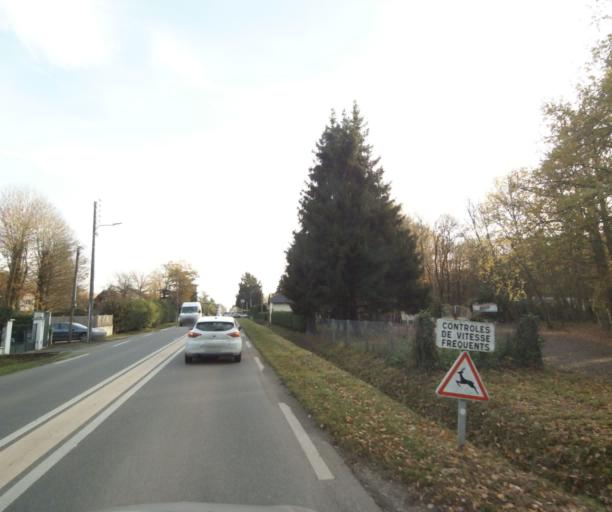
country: FR
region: Ile-de-France
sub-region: Departement du Val-d'Oise
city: Courdimanche
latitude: 49.0082
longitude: 2.0064
